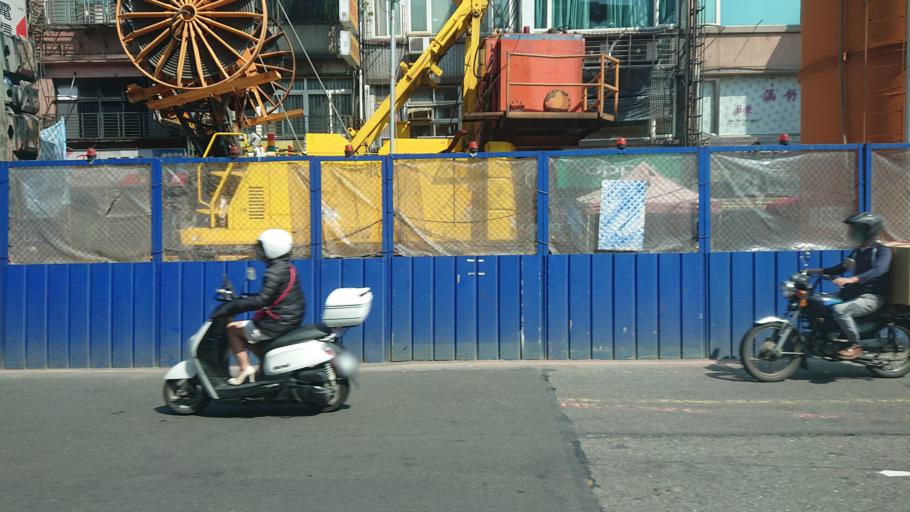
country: TW
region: Taipei
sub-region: Taipei
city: Banqiao
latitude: 25.0258
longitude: 121.5005
